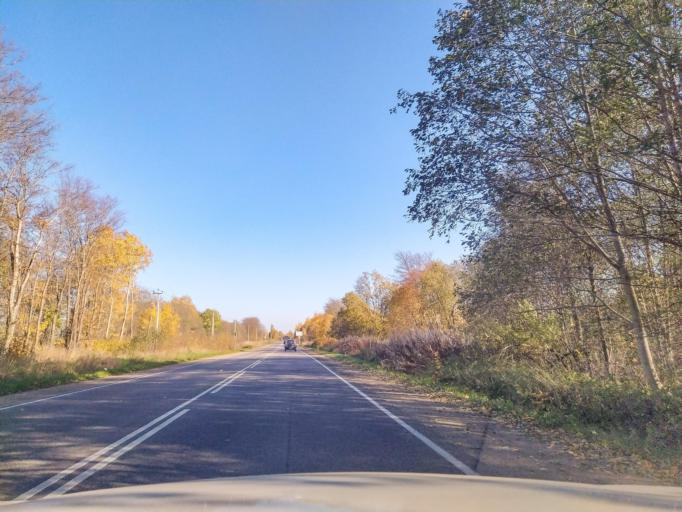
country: RU
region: Leningrad
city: Rozhdestveno
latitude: 59.3460
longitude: 29.9851
